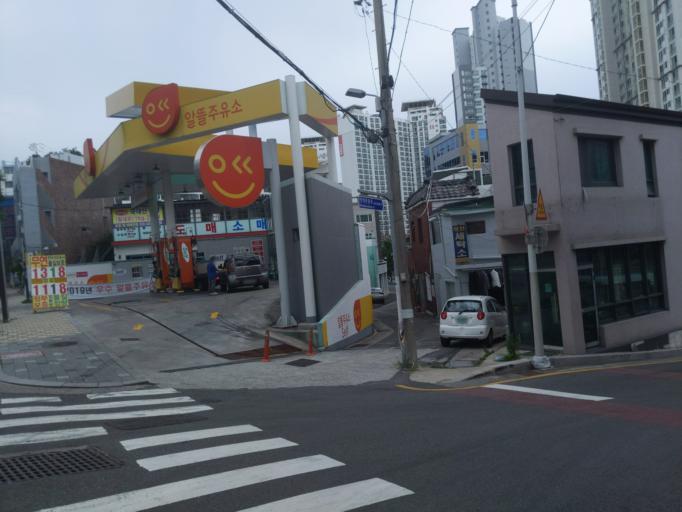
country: KR
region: Busan
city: Busan
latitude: 35.1592
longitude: 129.1286
